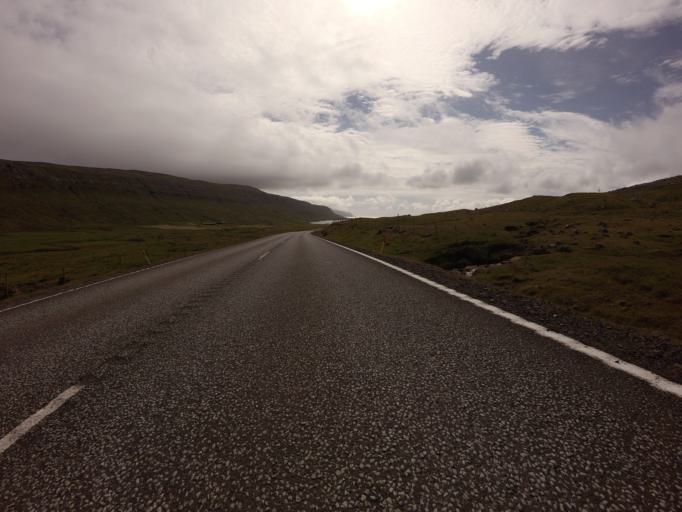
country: FO
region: Sandoy
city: Sandur
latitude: 61.8672
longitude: -6.8429
